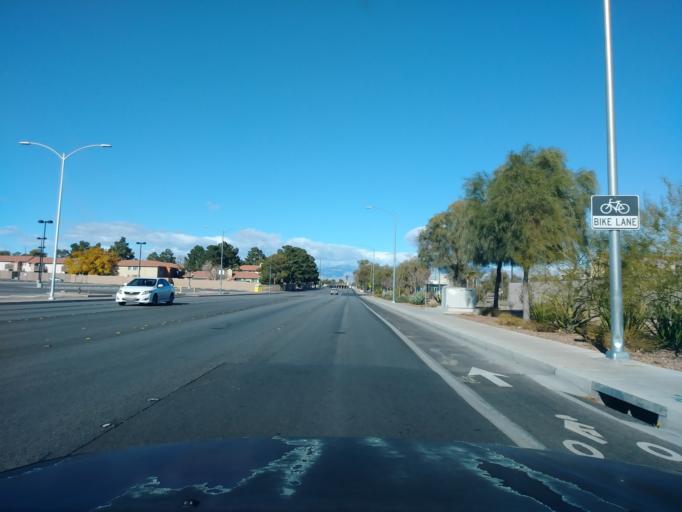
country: US
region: Nevada
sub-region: Clark County
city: Spring Valley
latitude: 36.1541
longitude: -115.2344
